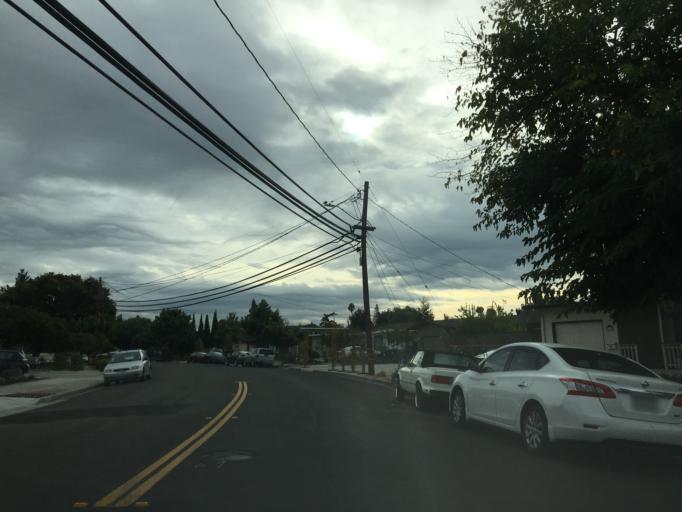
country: US
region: California
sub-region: Santa Clara County
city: Sunnyvale
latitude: 37.3904
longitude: -122.0232
